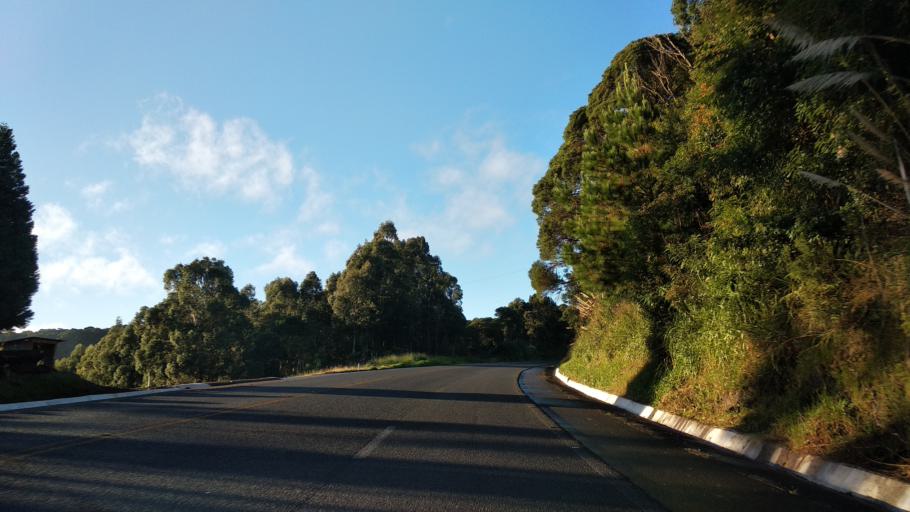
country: BR
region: Santa Catarina
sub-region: Curitibanos
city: Curitibanos
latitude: -27.6077
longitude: -50.7187
